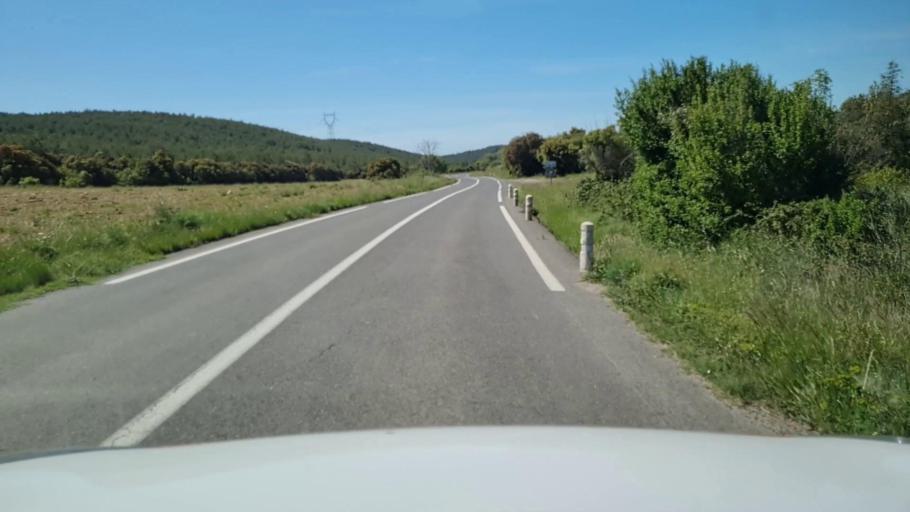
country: FR
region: Languedoc-Roussillon
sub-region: Departement du Gard
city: Villevieille
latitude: 43.8650
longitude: 4.0992
